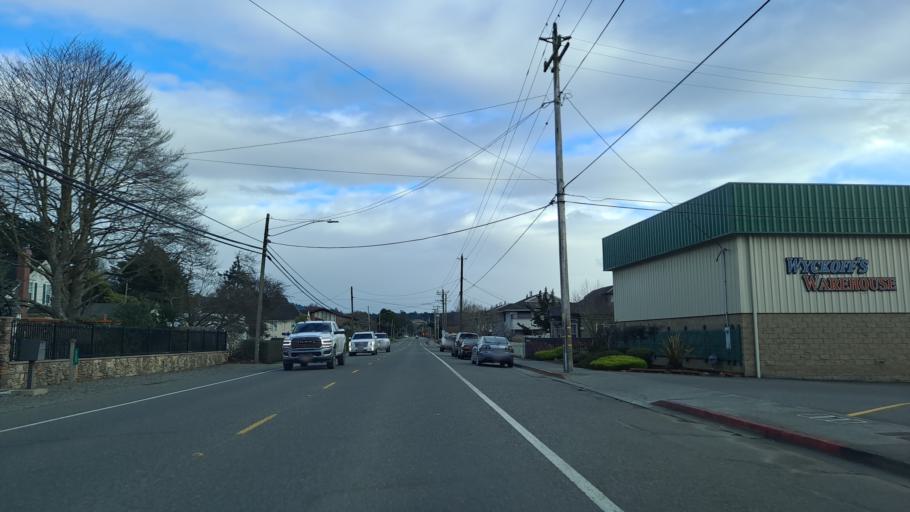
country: US
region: California
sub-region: Humboldt County
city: Fortuna
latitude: 40.5959
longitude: -124.1449
